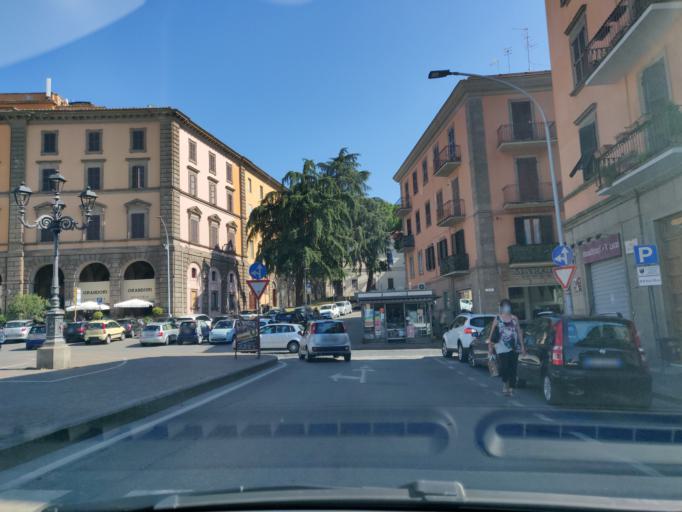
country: IT
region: Latium
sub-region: Provincia di Viterbo
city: Viterbo
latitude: 42.4217
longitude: 12.1054
